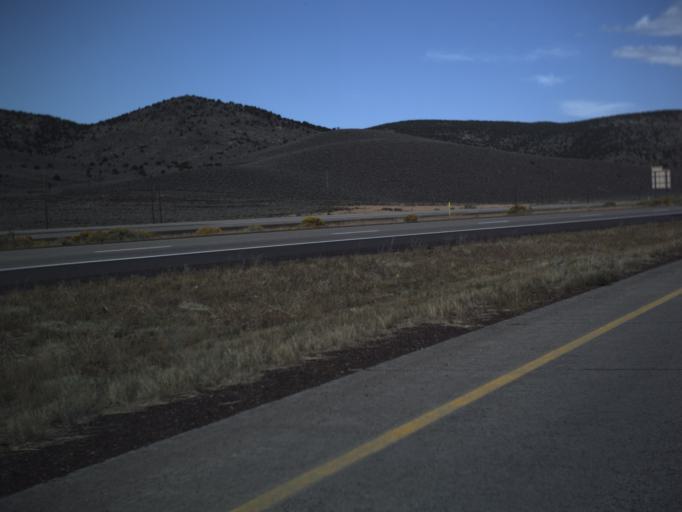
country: US
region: Utah
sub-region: Beaver County
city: Beaver
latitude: 38.0745
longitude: -112.6863
